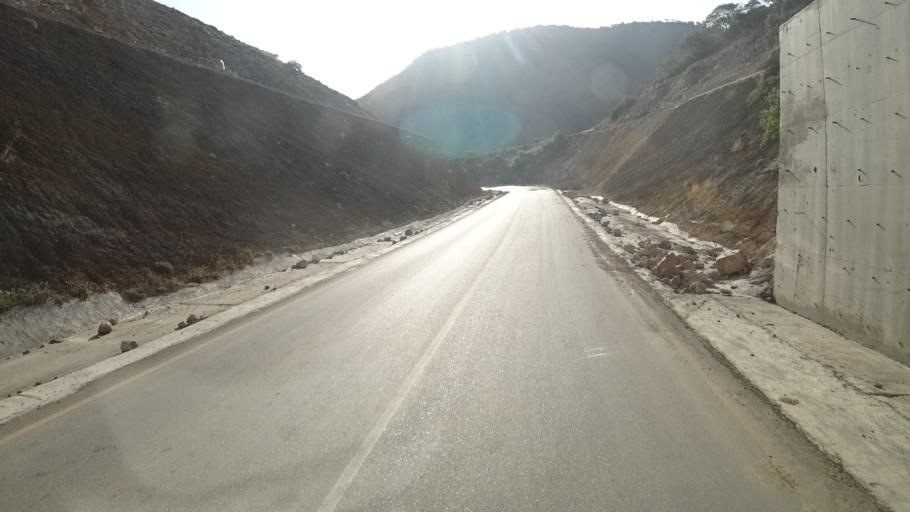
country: OM
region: Zufar
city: Salalah
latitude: 17.0560
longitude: 54.6122
